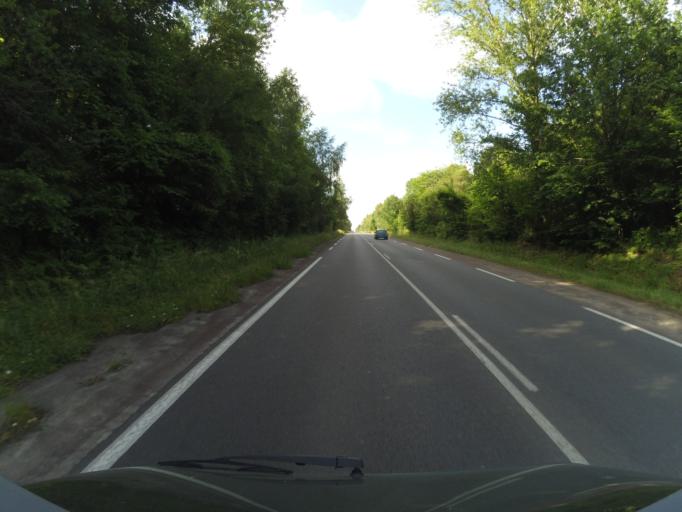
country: FR
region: Poitou-Charentes
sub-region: Departement de la Charente-Maritime
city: Le Gua
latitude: 45.7777
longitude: -0.9362
